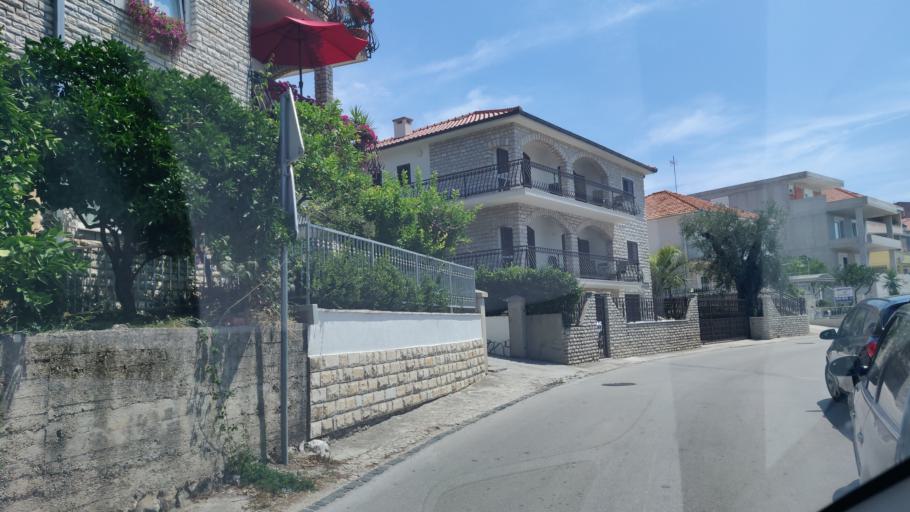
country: HR
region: Splitsko-Dalmatinska
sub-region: Grad Trogir
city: Trogir
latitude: 43.5070
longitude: 16.2593
